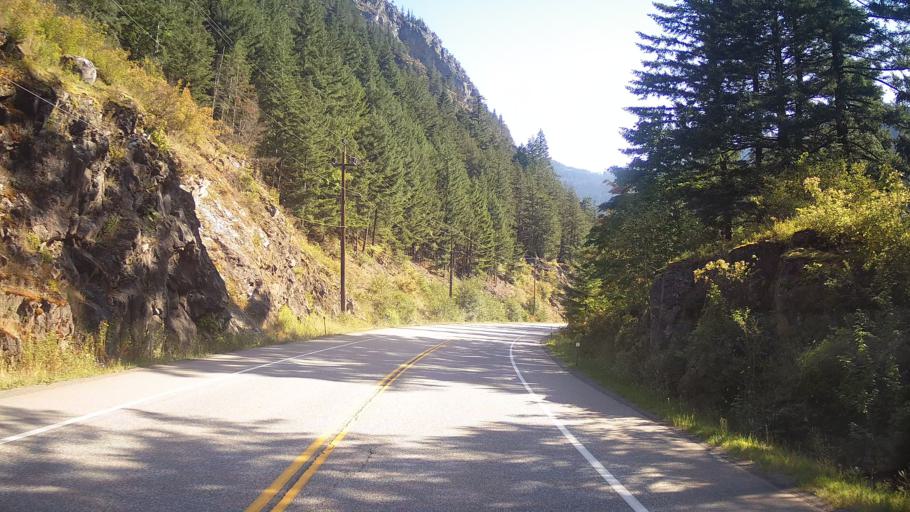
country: CA
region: British Columbia
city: Hope
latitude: 49.6146
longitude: -121.4109
